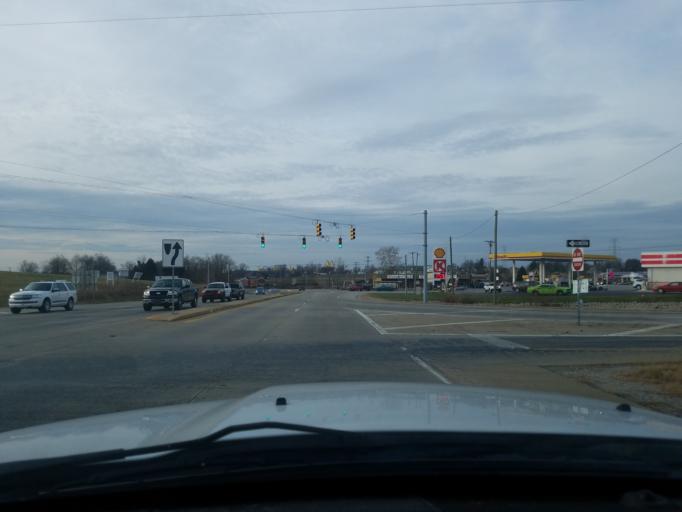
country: US
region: Indiana
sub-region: Floyd County
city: Georgetown
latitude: 38.2879
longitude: -85.9125
